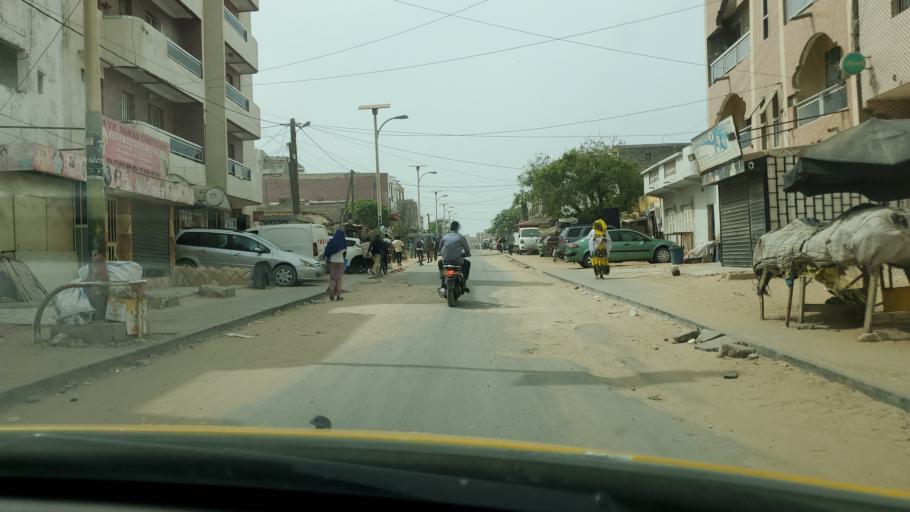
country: SN
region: Dakar
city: Pikine
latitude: 14.7712
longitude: -17.3941
